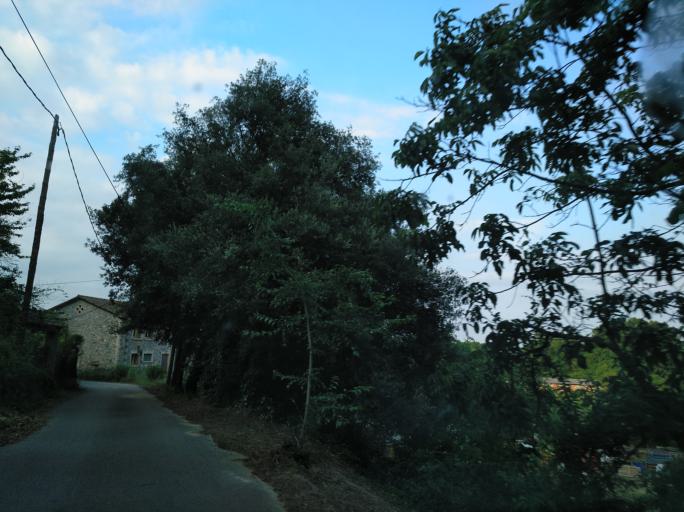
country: ES
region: Catalonia
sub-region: Provincia de Girona
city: la Cellera de Ter
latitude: 41.9566
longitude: 2.6213
